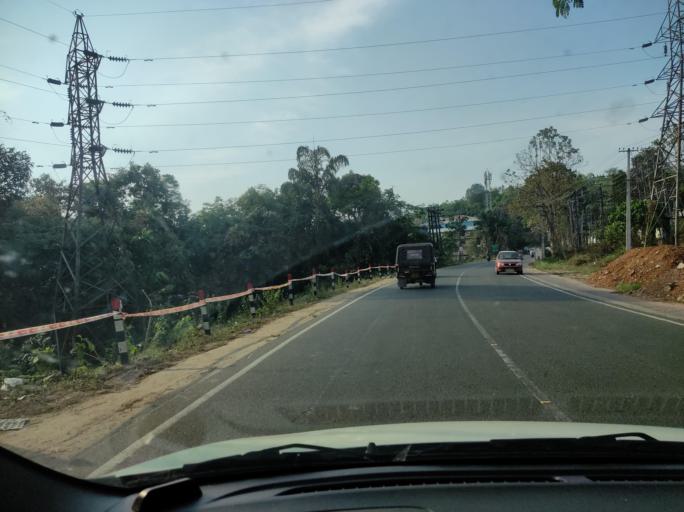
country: IN
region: Kerala
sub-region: Kottayam
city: Kottayam
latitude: 9.6314
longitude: 76.5248
